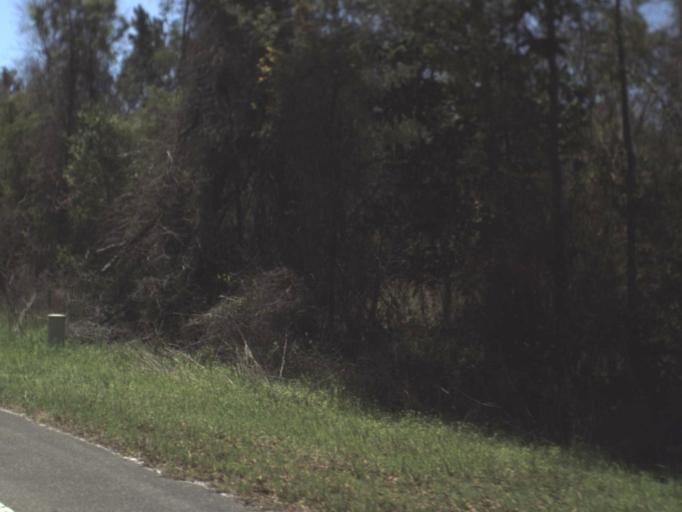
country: US
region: Florida
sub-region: Leon County
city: Woodville
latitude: 30.2474
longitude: -84.2333
